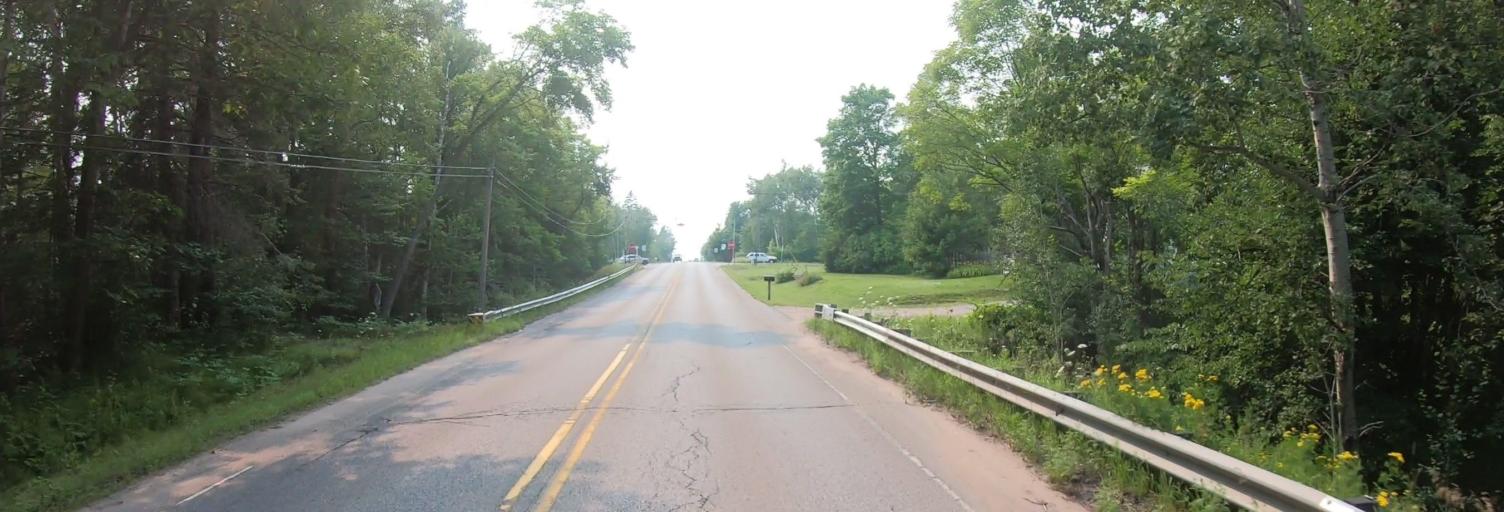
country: US
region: Michigan
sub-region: Chippewa County
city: Sault Ste. Marie
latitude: 46.4631
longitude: -84.3363
